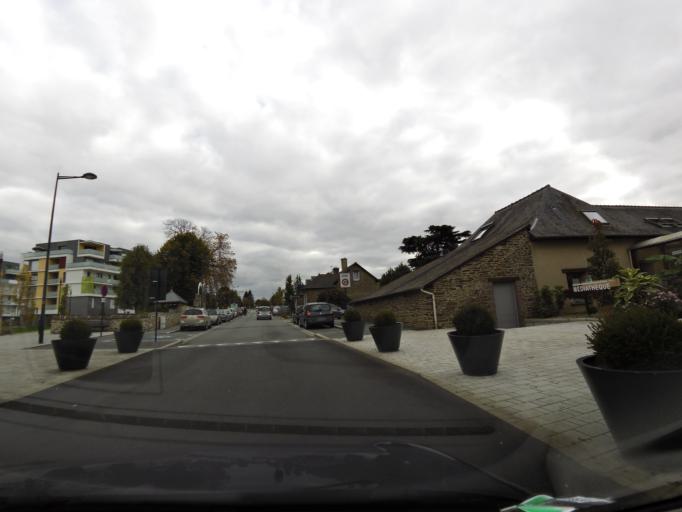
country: FR
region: Brittany
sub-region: Departement d'Ille-et-Vilaine
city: Chantepie
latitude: 48.0872
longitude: -1.6164
